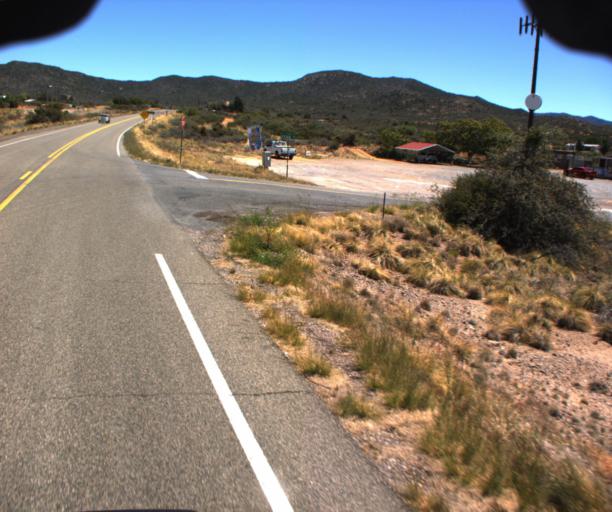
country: US
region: Arizona
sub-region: Yavapai County
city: Prescott
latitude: 34.4237
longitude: -112.5900
